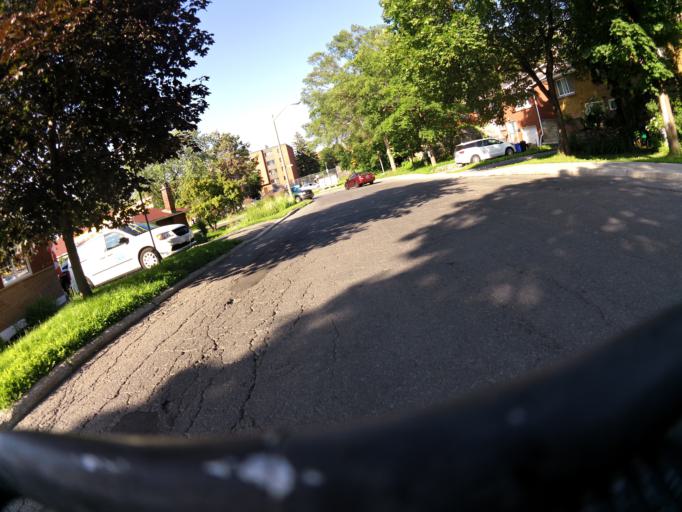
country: CA
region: Ontario
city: Ottawa
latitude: 45.3753
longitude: -75.7362
